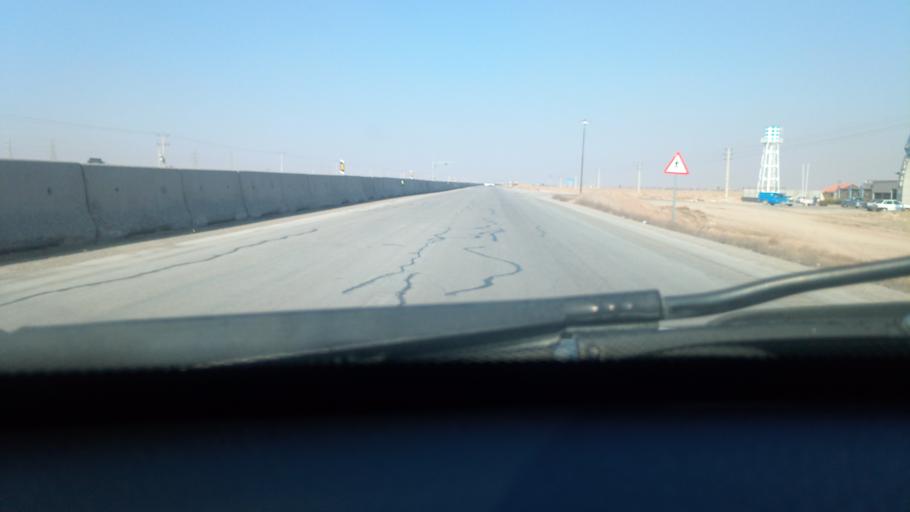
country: IR
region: Razavi Khorasan
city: Quchan
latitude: 36.9665
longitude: 58.6430
